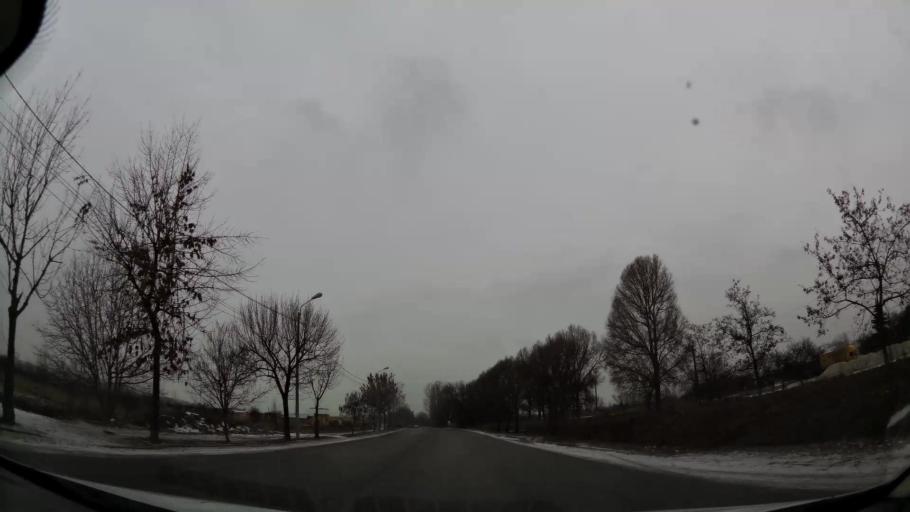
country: RO
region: Dambovita
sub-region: Municipiul Targoviste
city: Targoviste
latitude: 44.9267
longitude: 25.4825
